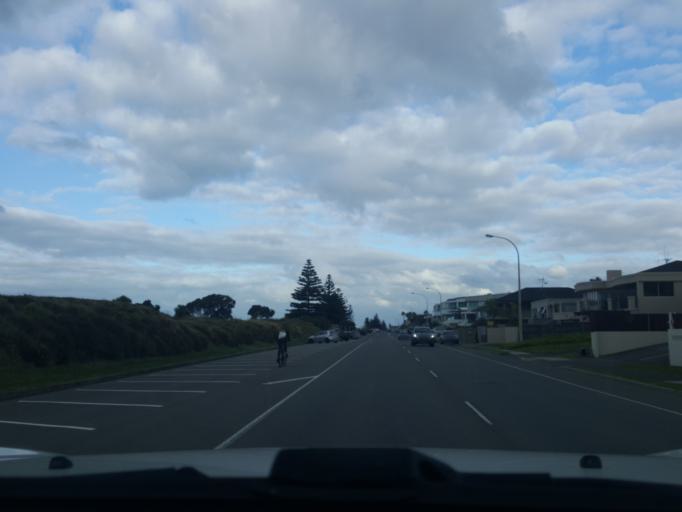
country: NZ
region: Bay of Plenty
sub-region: Tauranga City
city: Tauranga
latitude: -37.6441
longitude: 176.1949
